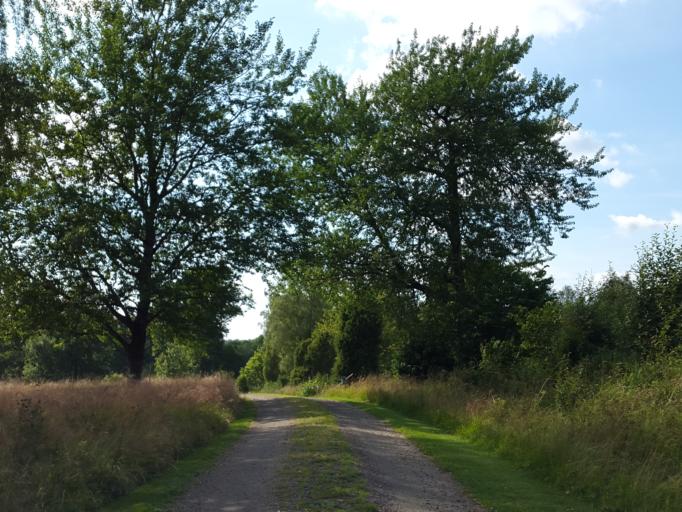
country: SE
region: Vaestra Goetaland
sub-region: Herrljunga Kommun
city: Herrljunga
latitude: 58.0223
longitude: 13.1227
